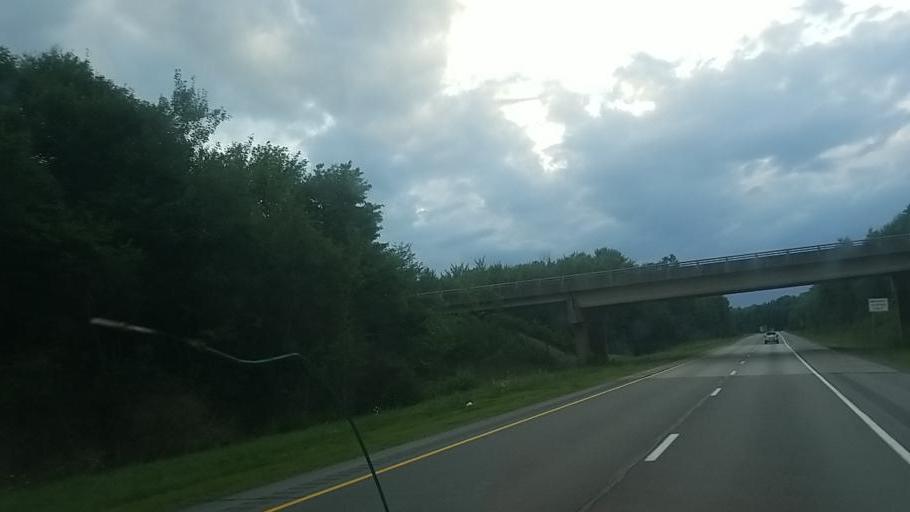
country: US
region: Pennsylvania
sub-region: Clearfield County
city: Curwensville
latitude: 41.1254
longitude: -78.5641
